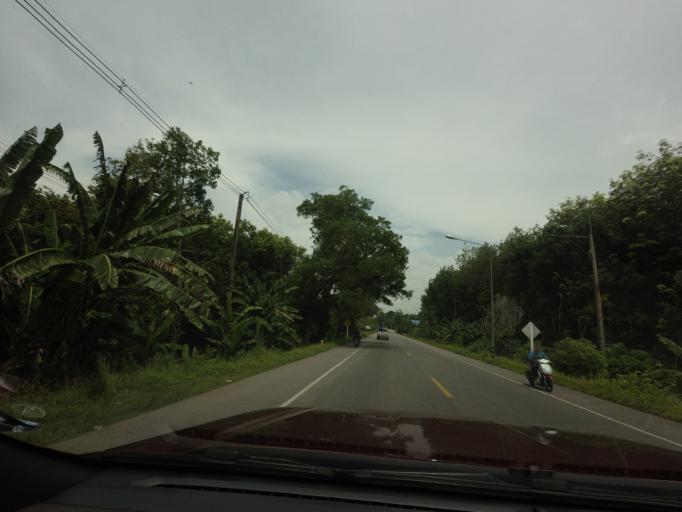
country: TH
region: Yala
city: Yala
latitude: 6.6057
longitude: 101.3040
